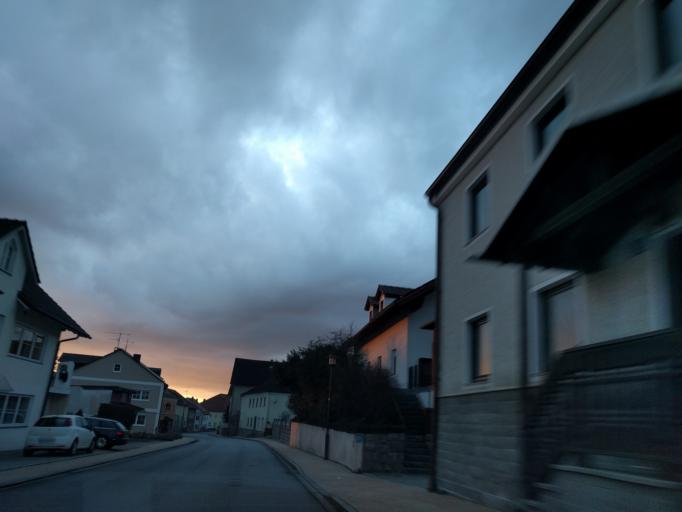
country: DE
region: Bavaria
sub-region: Lower Bavaria
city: Winzer
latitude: 48.7265
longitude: 13.0700
